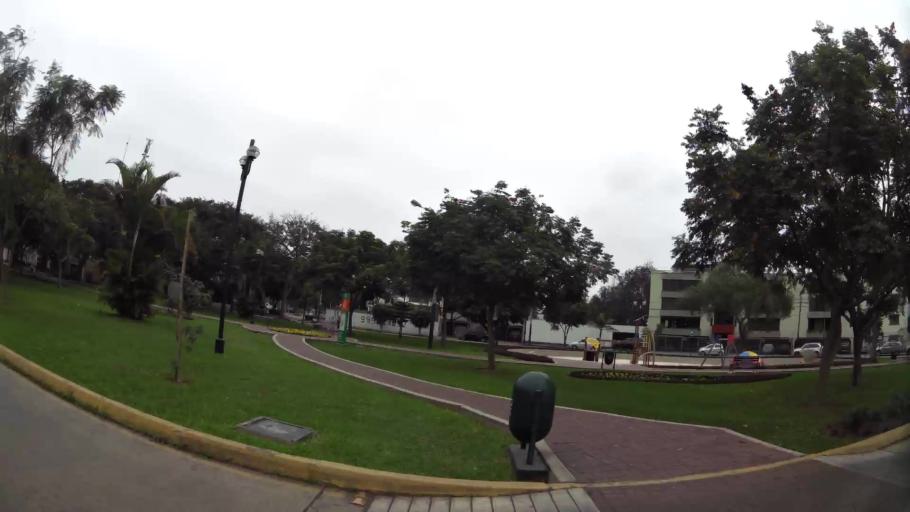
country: PE
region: Lima
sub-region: Lima
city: San Luis
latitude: -12.1010
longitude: -77.0164
